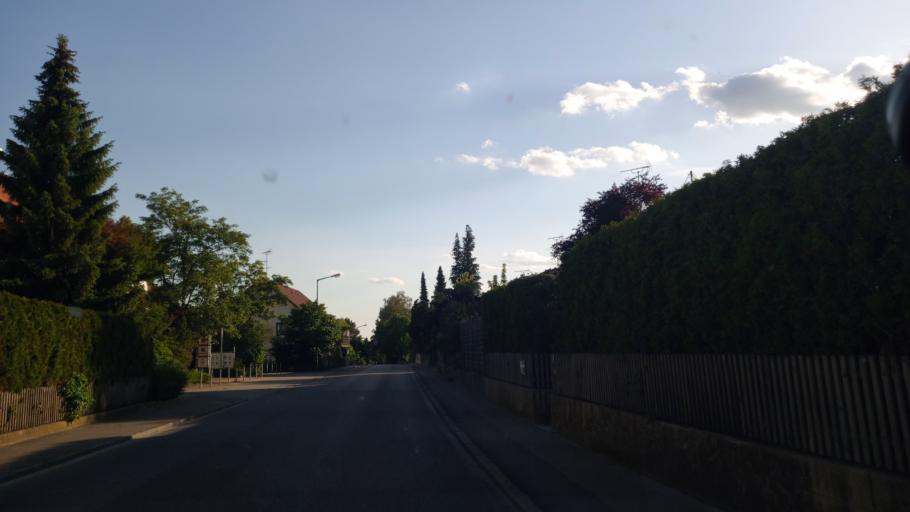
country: DE
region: Bavaria
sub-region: Upper Bavaria
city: Weichs
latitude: 48.3792
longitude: 11.4116
